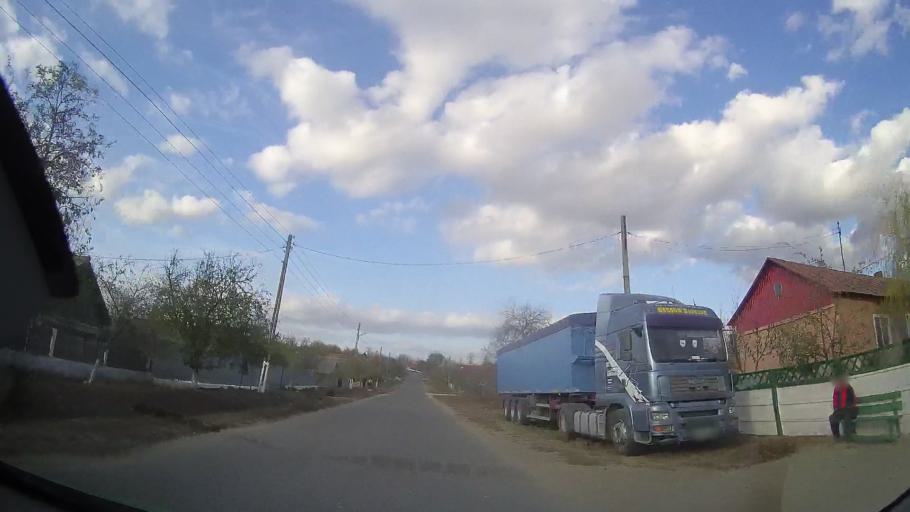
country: RO
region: Constanta
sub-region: Comuna Cerchezu
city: Cerchezu
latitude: 43.8581
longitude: 28.1013
